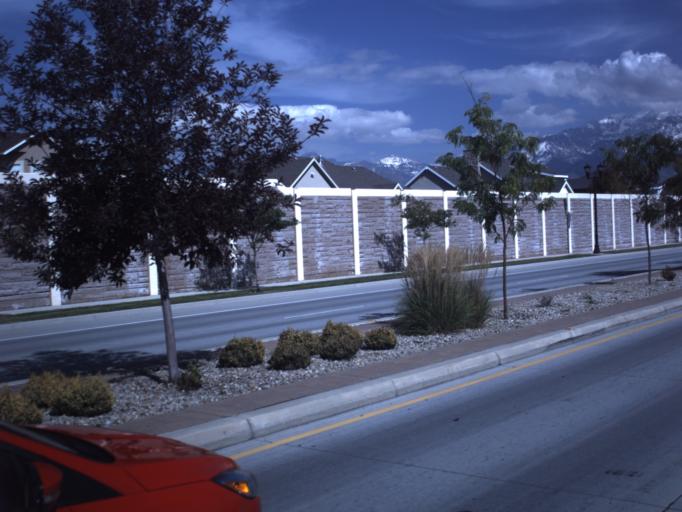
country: US
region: Utah
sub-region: Salt Lake County
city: South Jordan
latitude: 40.5442
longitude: -111.9212
